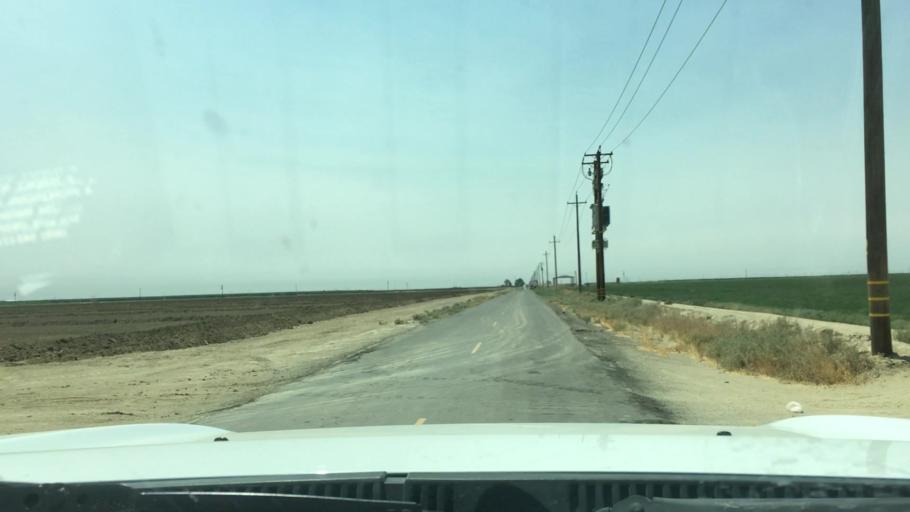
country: US
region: California
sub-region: Tulare County
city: Alpaugh
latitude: 35.7538
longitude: -119.4369
